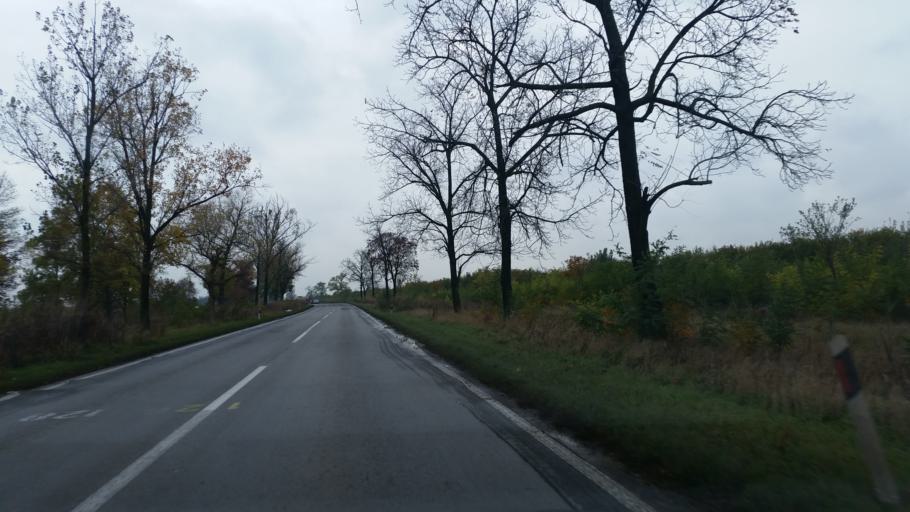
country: RS
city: Ecka
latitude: 45.3393
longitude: 20.4323
